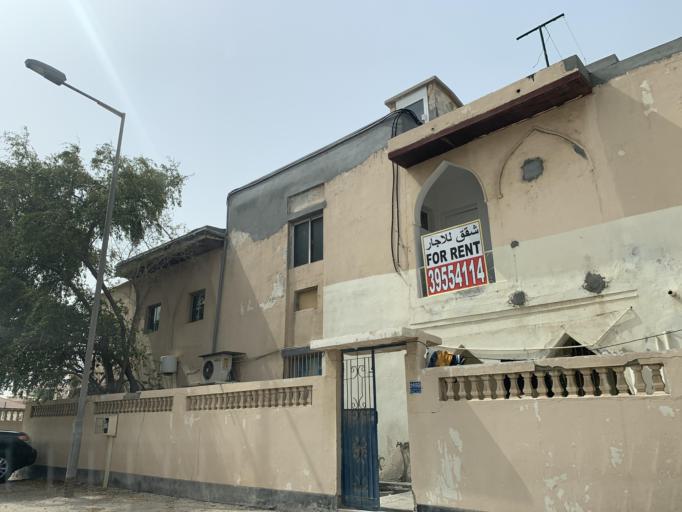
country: BH
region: Northern
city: Madinat `Isa
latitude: 26.1691
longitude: 50.5464
